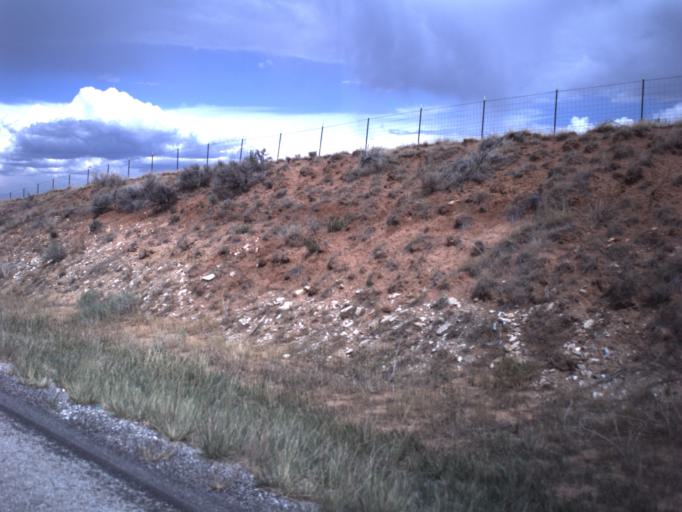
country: US
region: Utah
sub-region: San Juan County
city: Monticello
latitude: 37.8259
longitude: -109.3369
